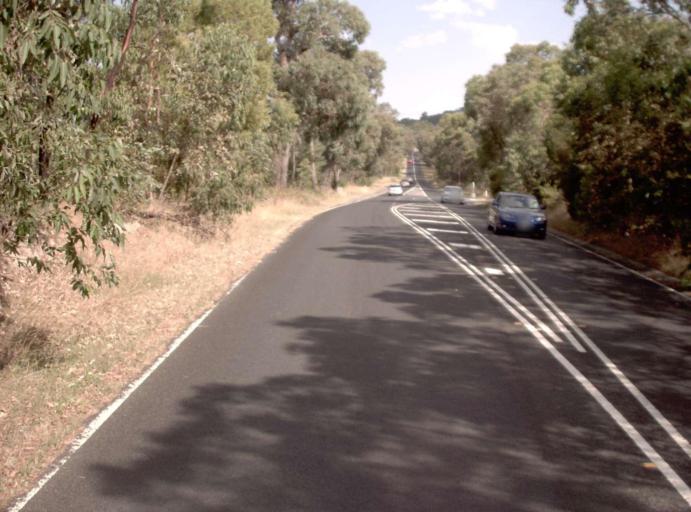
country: AU
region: Victoria
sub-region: Yarra Ranges
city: Lysterfield
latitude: -37.9178
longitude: 145.2772
